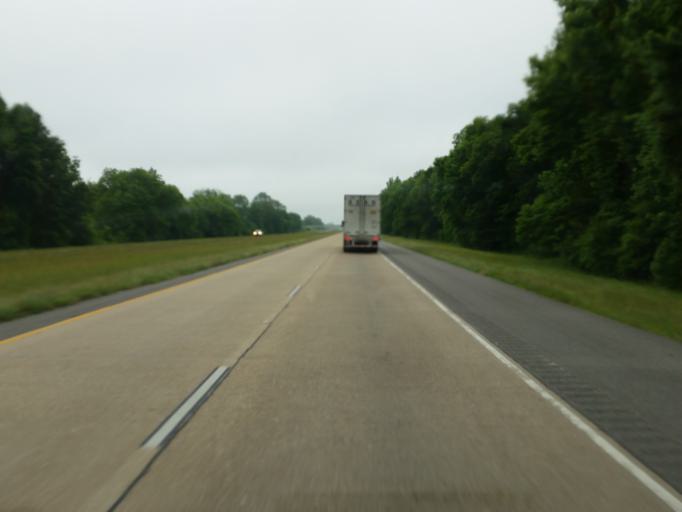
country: US
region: Louisiana
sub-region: Madison Parish
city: Tallulah
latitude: 32.3701
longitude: -91.1398
